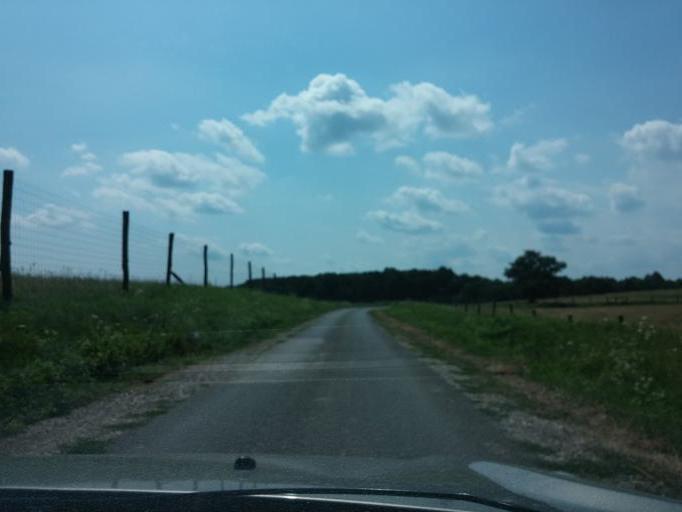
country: HU
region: Somogy
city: Kaposvar
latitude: 46.2548
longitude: 17.8211
